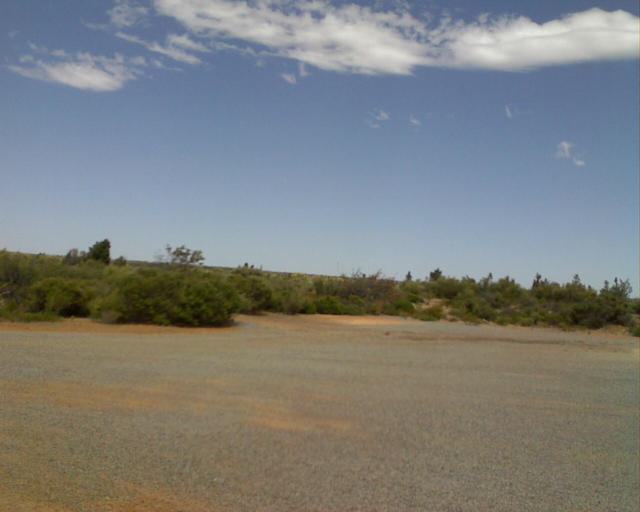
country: AU
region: Western Australia
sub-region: Moora
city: Moora
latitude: -30.0609
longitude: 115.6678
